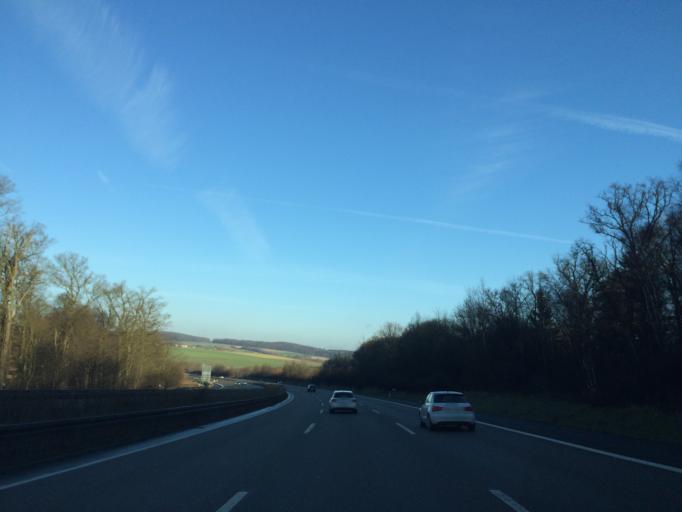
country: DE
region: Hesse
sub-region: Regierungsbezirk Kassel
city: Malsfeld
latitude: 51.0454
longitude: 9.4964
